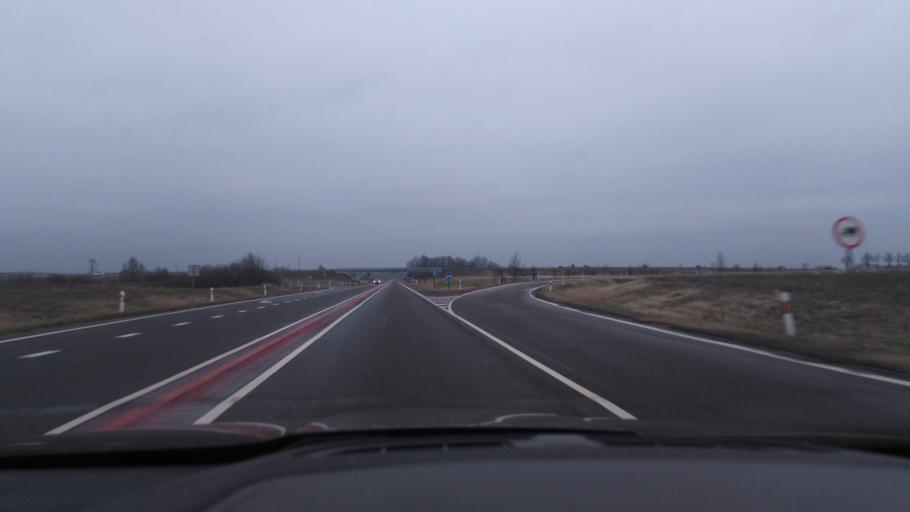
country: LT
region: Marijampoles apskritis
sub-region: Marijampole Municipality
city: Marijampole
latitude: 54.5705
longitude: 23.2939
